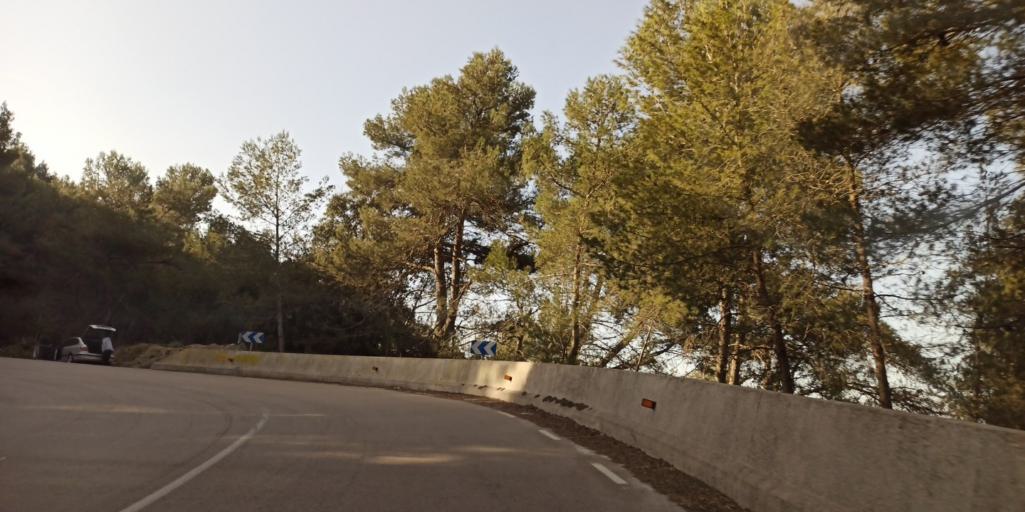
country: ES
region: Catalonia
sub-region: Provincia de Barcelona
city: Castelloli
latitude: 41.5968
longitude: 1.7315
